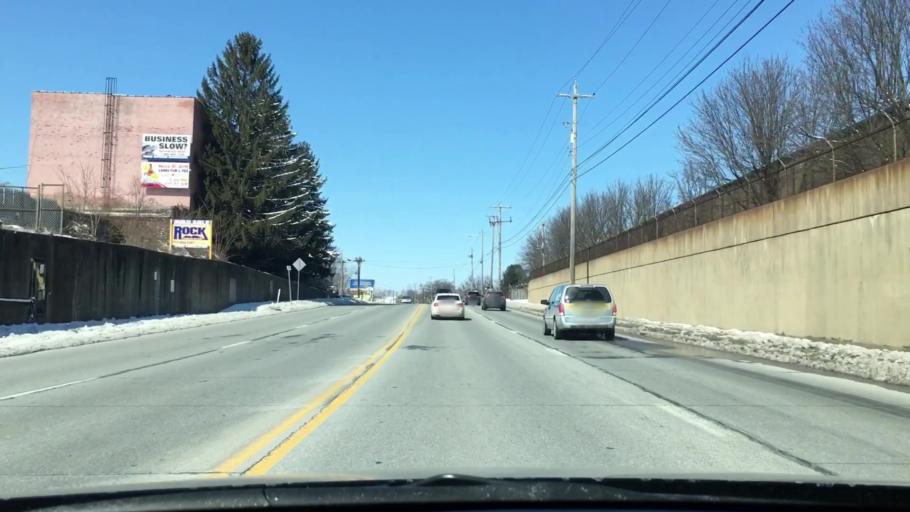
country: US
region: Pennsylvania
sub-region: York County
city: West York
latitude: 39.9458
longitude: -76.7421
